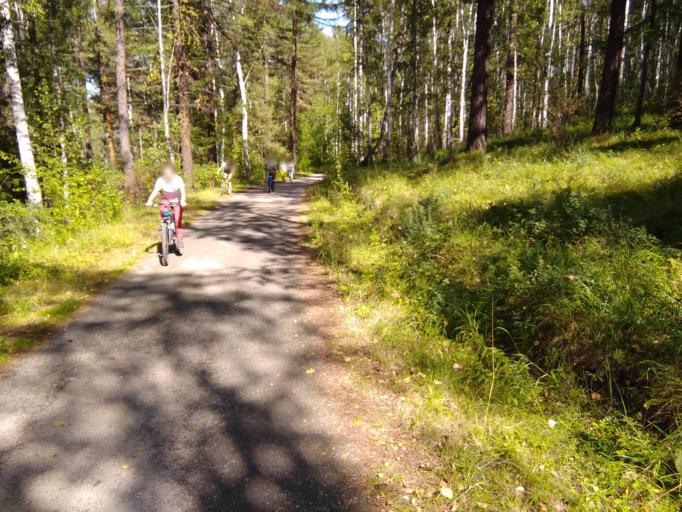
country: RU
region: Bashkortostan
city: Abzakovo
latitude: 53.8141
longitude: 58.6036
